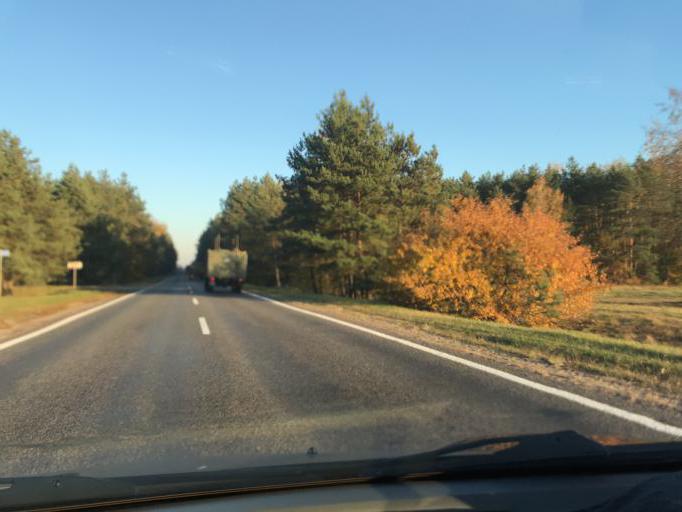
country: BY
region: Minsk
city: Staryya Darohi
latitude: 53.0444
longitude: 28.1285
